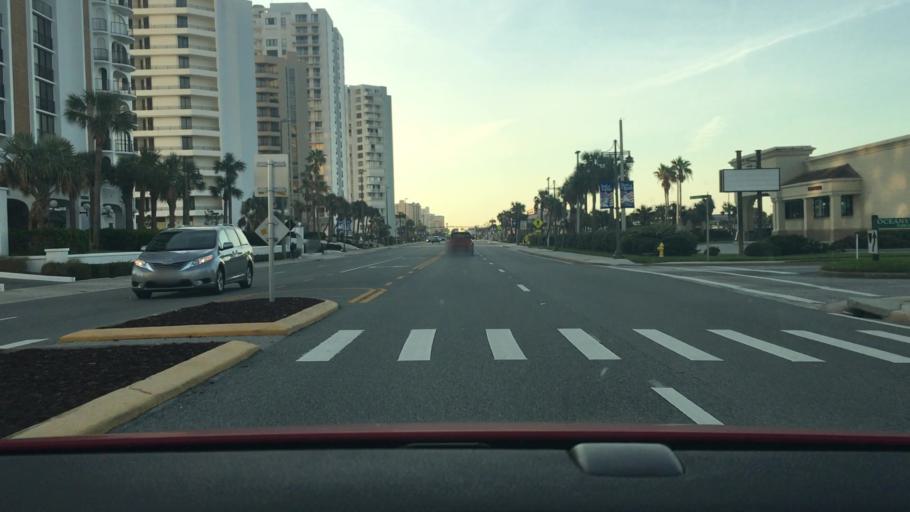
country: US
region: Florida
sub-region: Volusia County
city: Daytona Beach Shores
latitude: 29.1692
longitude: -80.9789
